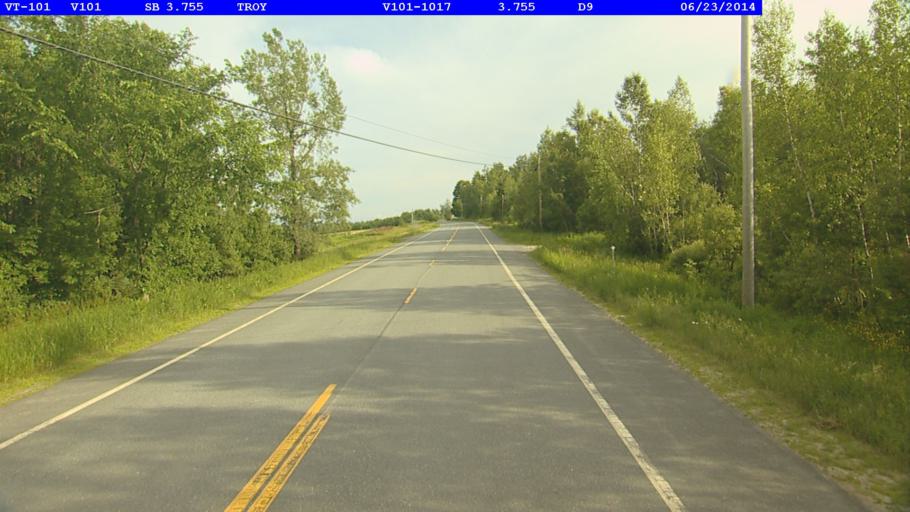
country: US
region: Vermont
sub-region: Orleans County
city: Newport
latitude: 44.9565
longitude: -72.4124
